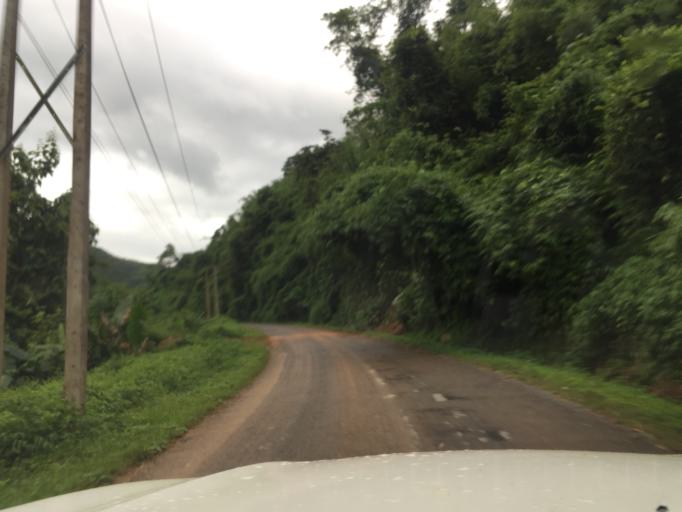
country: LA
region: Oudomxai
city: Muang La
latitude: 20.9652
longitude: 102.2208
